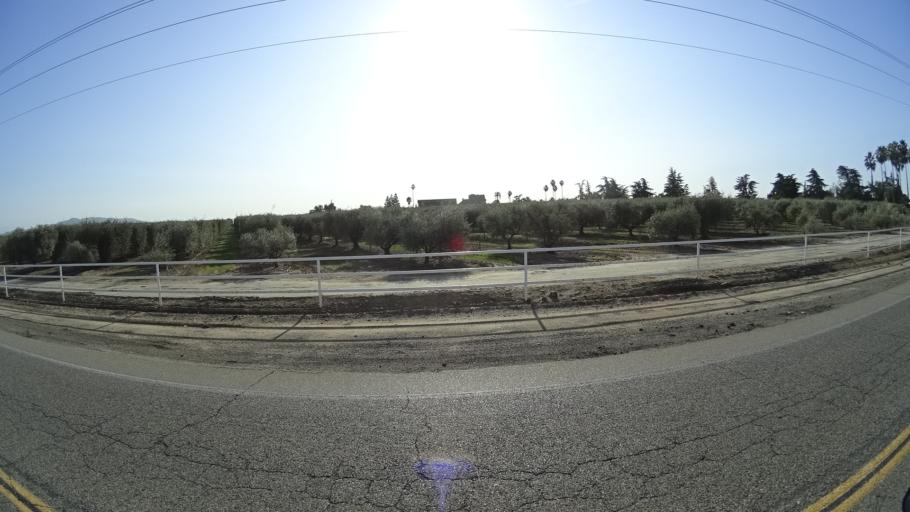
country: US
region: California
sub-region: Fresno County
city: Clovis
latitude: 36.9067
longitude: -119.7319
